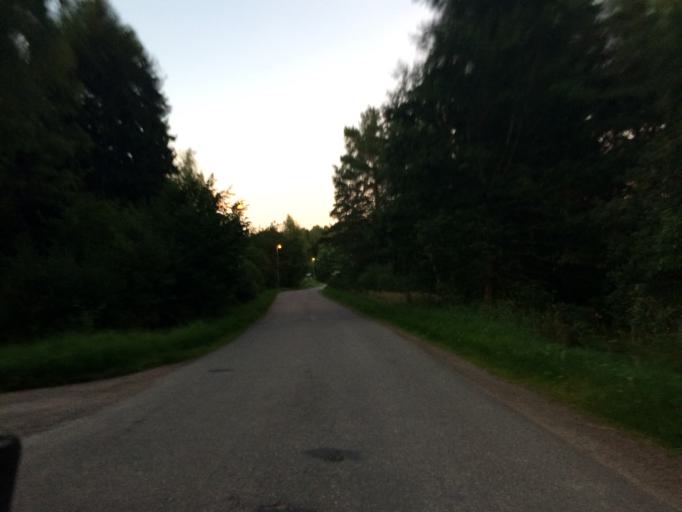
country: SE
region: Soedermanland
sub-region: Eskilstuna Kommun
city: Kvicksund
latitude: 59.4450
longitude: 16.3132
